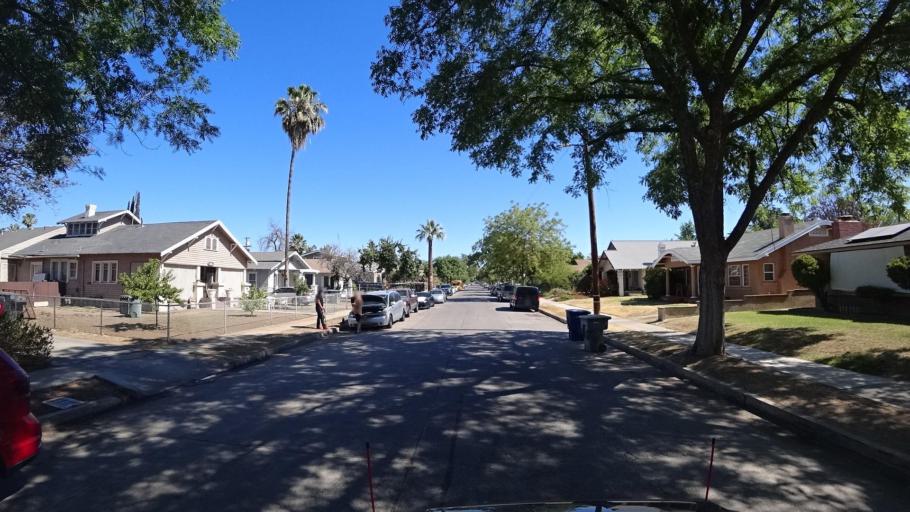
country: US
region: California
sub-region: Fresno County
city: Fresno
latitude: 36.7526
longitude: -119.8052
